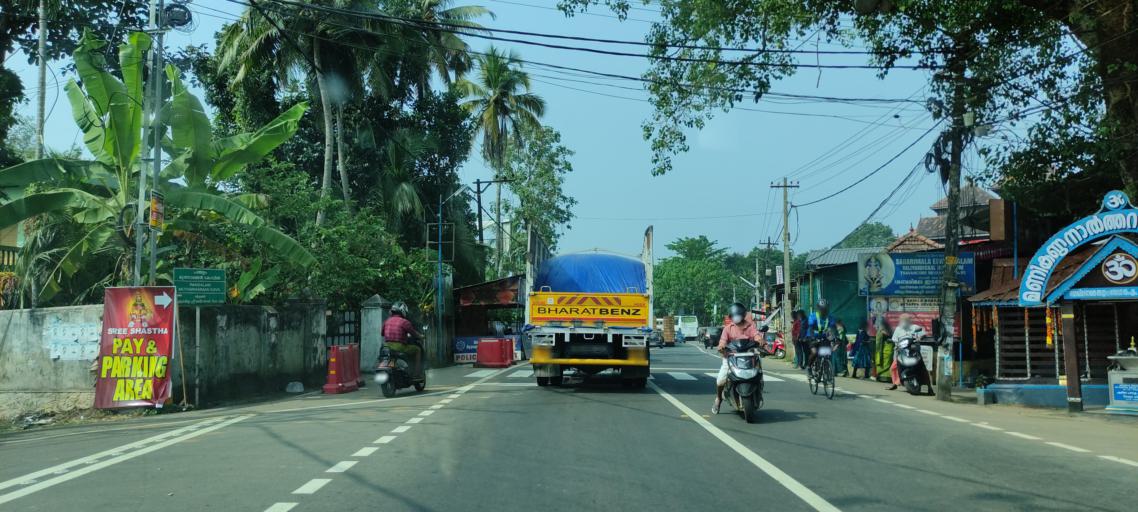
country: IN
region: Kerala
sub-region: Pattanamtitta
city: Adur
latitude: 9.2321
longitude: 76.6749
